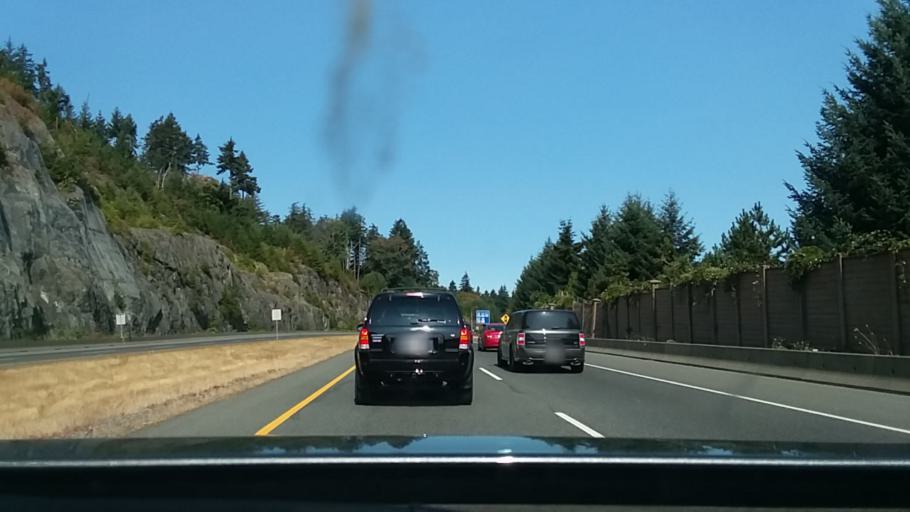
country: CA
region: British Columbia
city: Nanaimo
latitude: 49.1643
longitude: -123.9765
